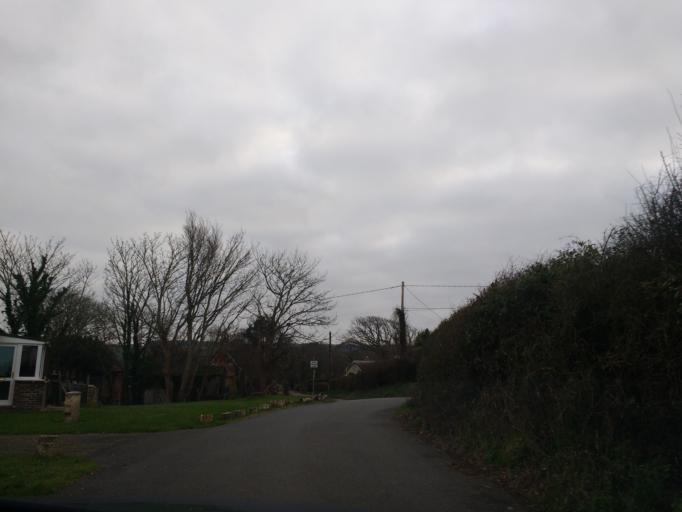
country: GB
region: England
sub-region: Isle of Wight
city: Shalfleet
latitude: 50.6882
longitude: -1.3952
